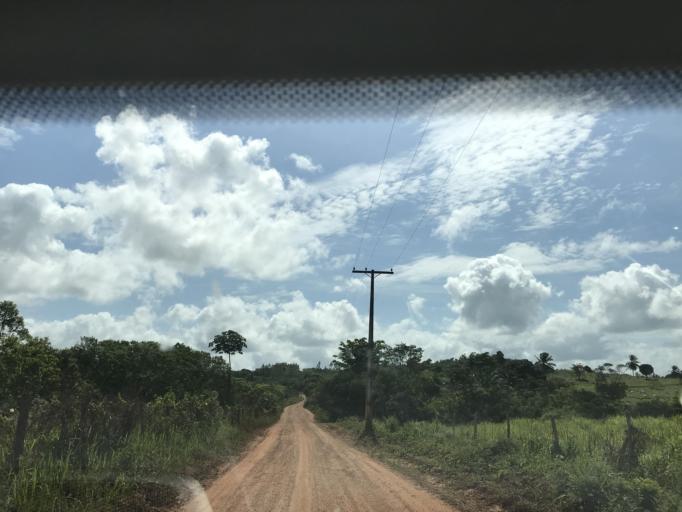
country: BR
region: Bahia
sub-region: Entre Rios
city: Entre Rios
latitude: -12.1860
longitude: -38.0525
